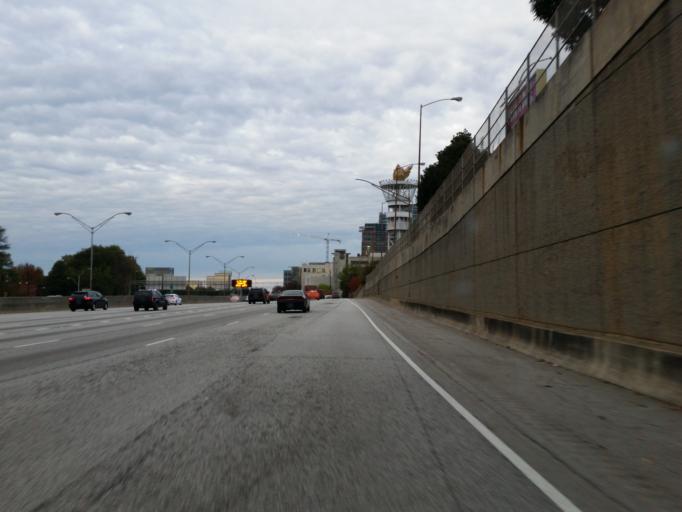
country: US
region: Georgia
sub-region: Fulton County
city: Atlanta
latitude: 33.7720
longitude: -84.3899
